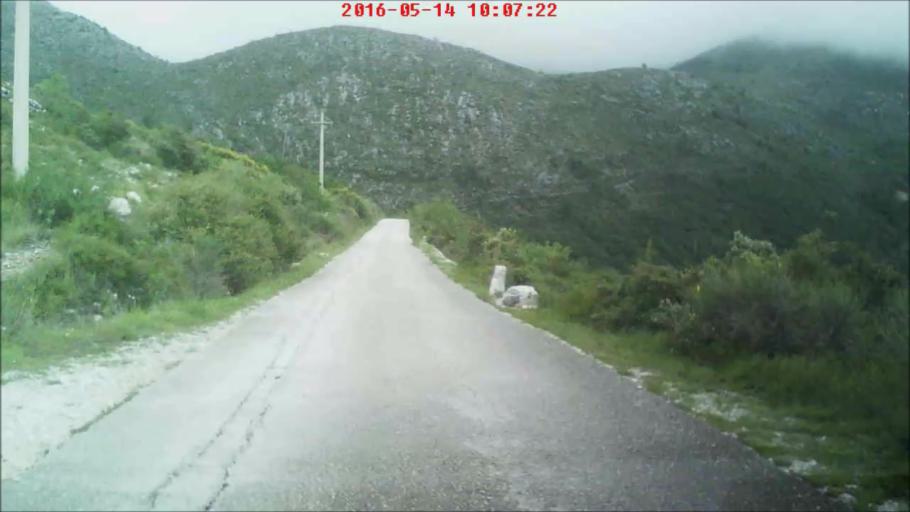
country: HR
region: Dubrovacko-Neretvanska
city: Podgora
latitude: 42.7482
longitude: 17.9291
